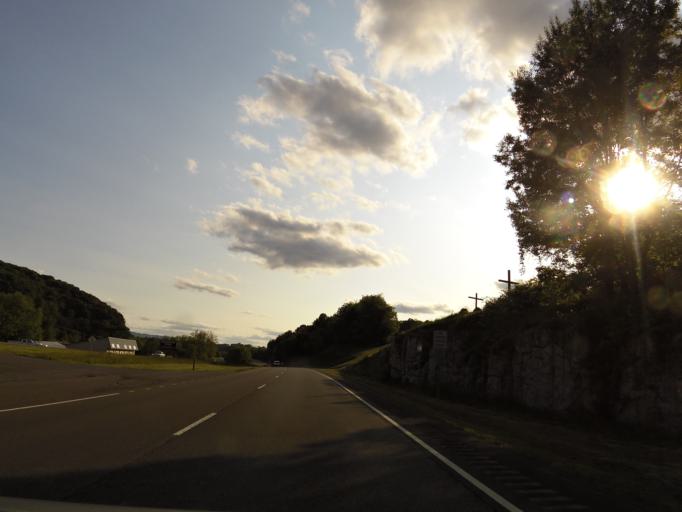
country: US
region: Virginia
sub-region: Russell County
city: Honaker
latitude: 36.9561
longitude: -81.9412
